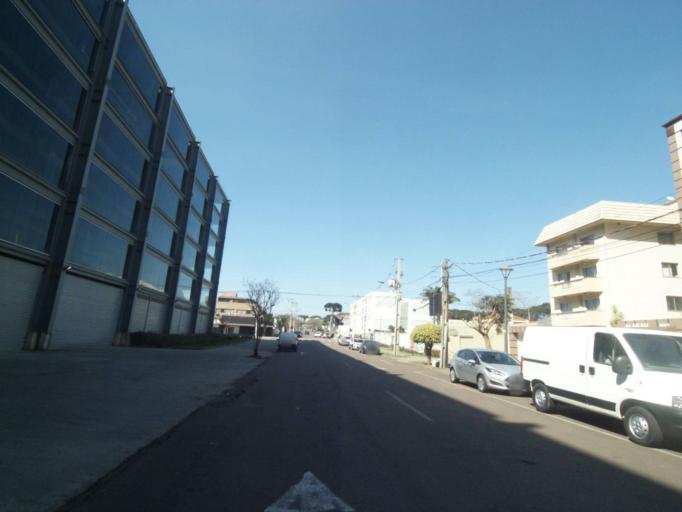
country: BR
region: Parana
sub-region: Curitiba
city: Curitiba
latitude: -25.4492
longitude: -49.2768
